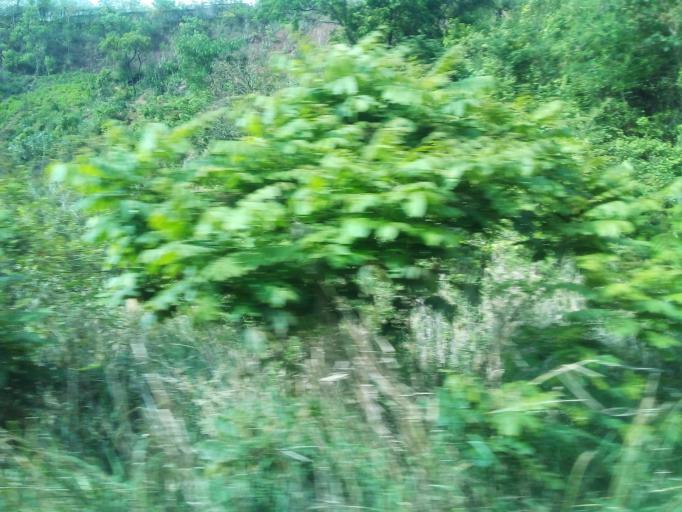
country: BR
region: Minas Gerais
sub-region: Santa Luzia
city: Santa Luzia
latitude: -19.8690
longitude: -43.8351
